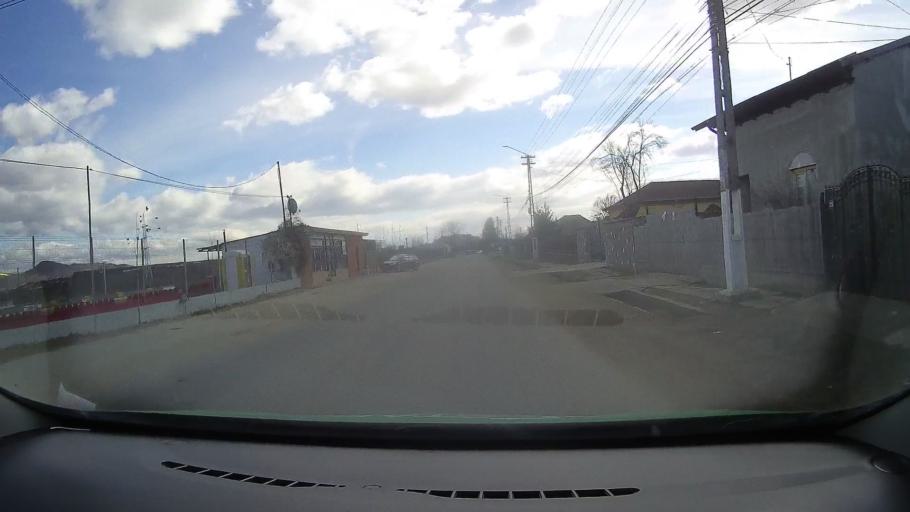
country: RO
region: Dambovita
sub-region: Comuna Doicesti
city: Doicesti
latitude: 44.9855
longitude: 25.3853
